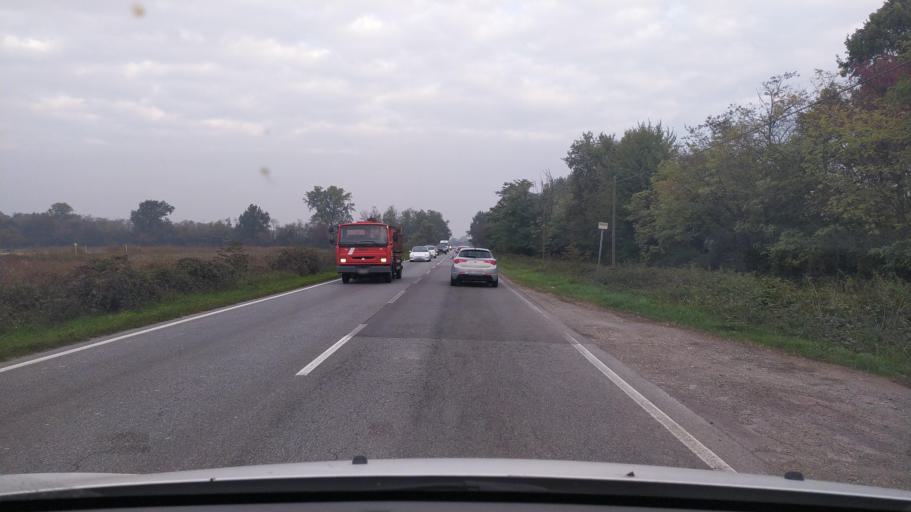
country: IT
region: Lombardy
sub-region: Citta metropolitana di Milano
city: Cisliano
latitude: 45.4407
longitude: 8.9730
